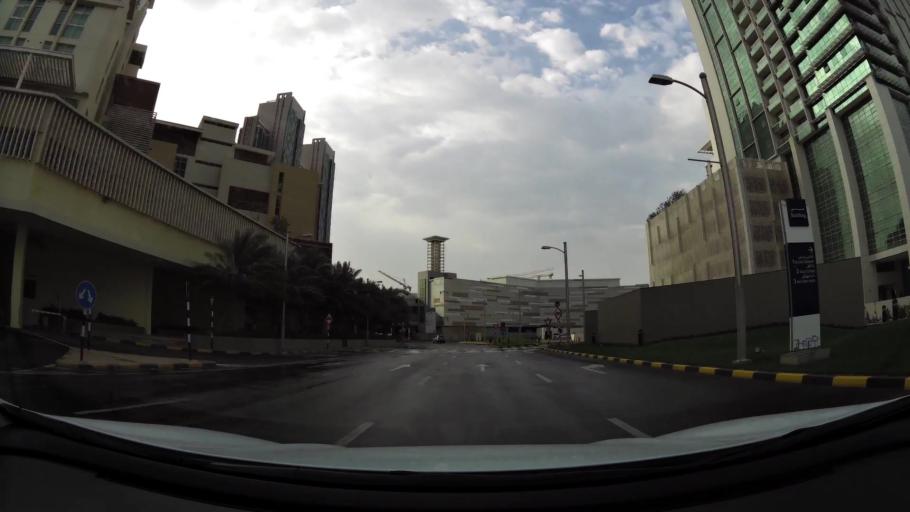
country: AE
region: Abu Dhabi
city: Abu Dhabi
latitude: 24.4922
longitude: 54.3935
